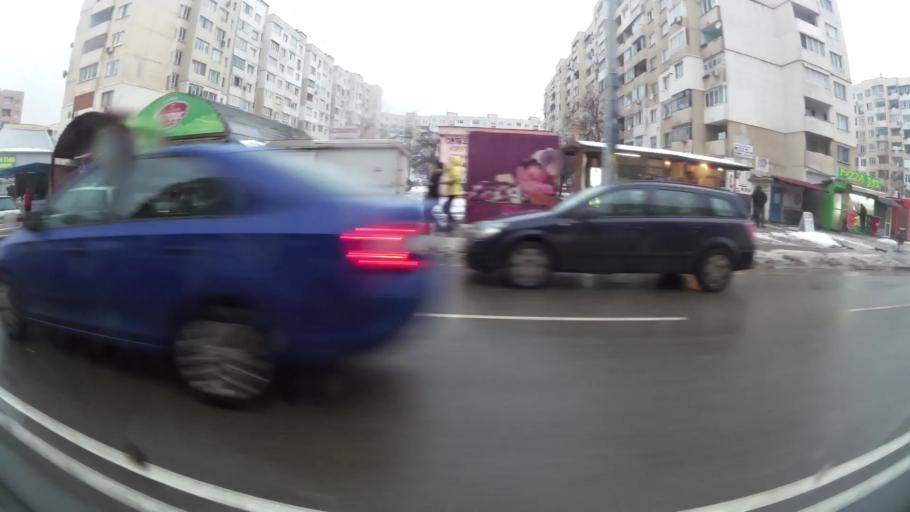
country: BG
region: Sofia-Capital
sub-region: Stolichna Obshtina
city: Sofia
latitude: 42.6891
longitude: 23.2549
